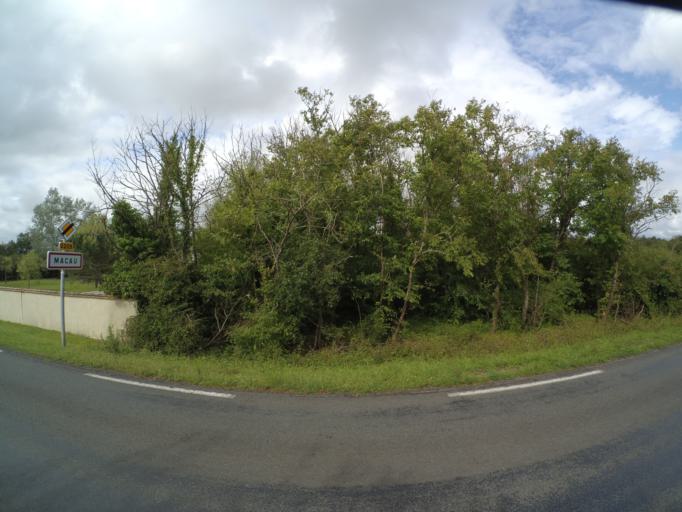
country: FR
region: Aquitaine
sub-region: Departement de la Gironde
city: Macau
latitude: 45.0036
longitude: -0.6048
